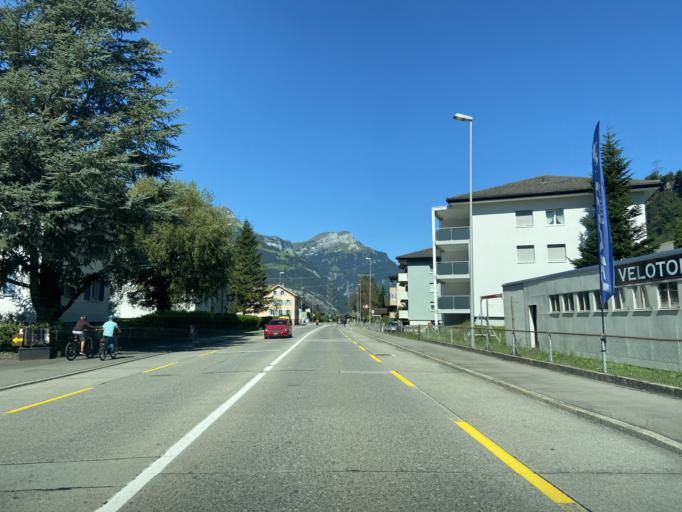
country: CH
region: Uri
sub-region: Uri
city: Altdorf
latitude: 46.8890
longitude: 8.6308
